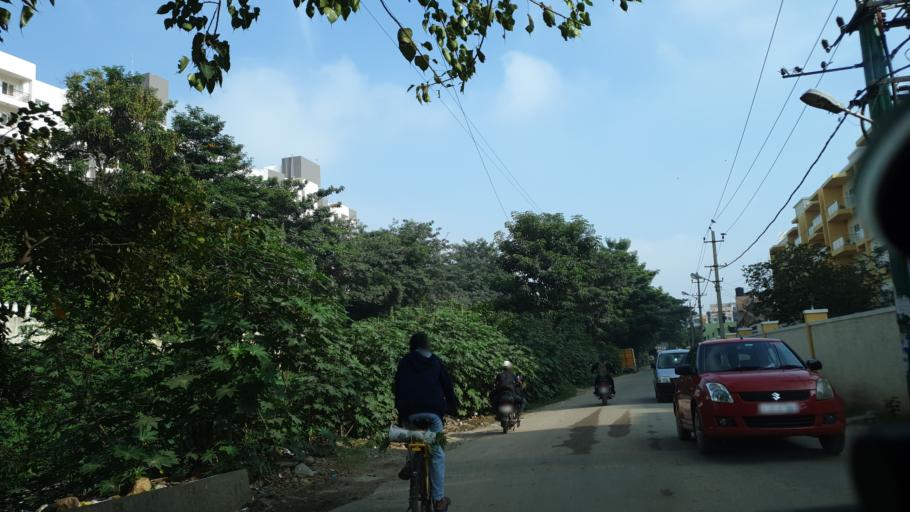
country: IN
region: Karnataka
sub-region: Bangalore Urban
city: Bangalore
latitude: 12.9575
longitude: 77.7047
